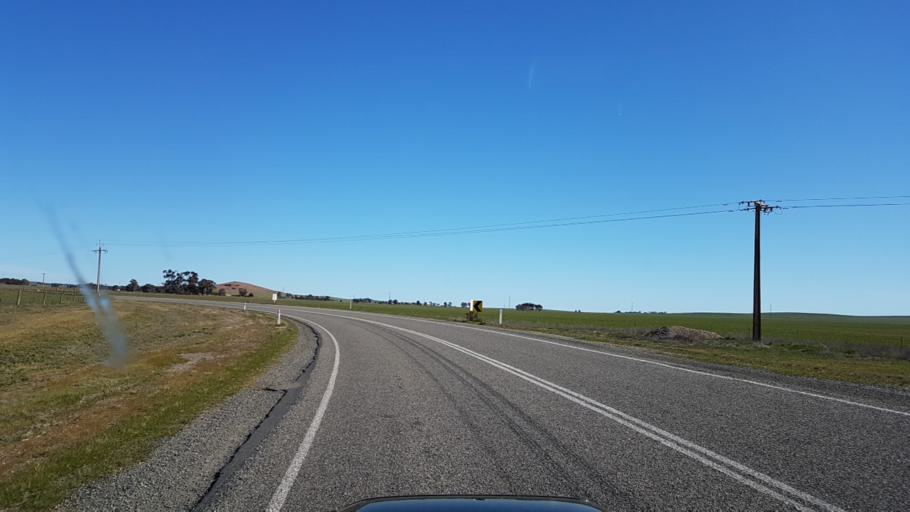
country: AU
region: South Australia
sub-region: Clare and Gilbert Valleys
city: Clare
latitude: -33.6836
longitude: 138.9060
